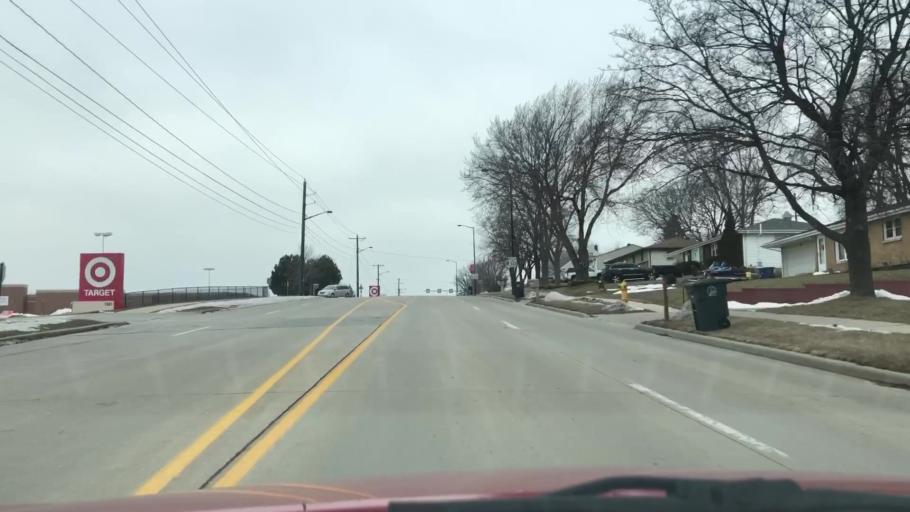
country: US
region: Wisconsin
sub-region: Brown County
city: Ashwaubenon
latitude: 44.4906
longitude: -88.0684
